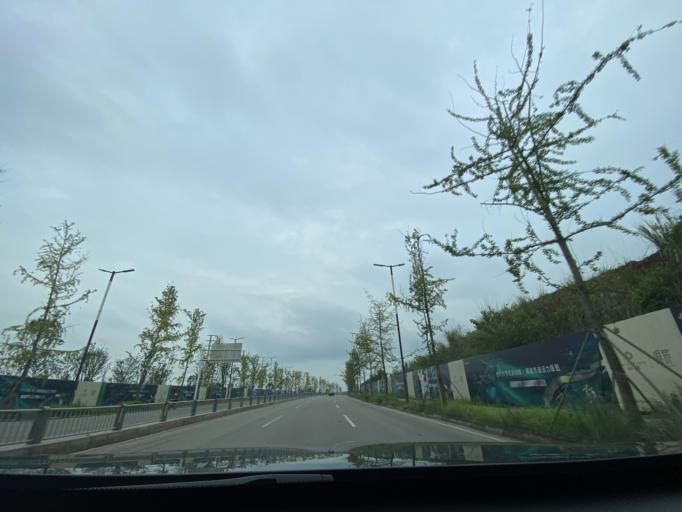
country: CN
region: Sichuan
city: Jiancheng
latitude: 30.4948
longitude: 104.4514
